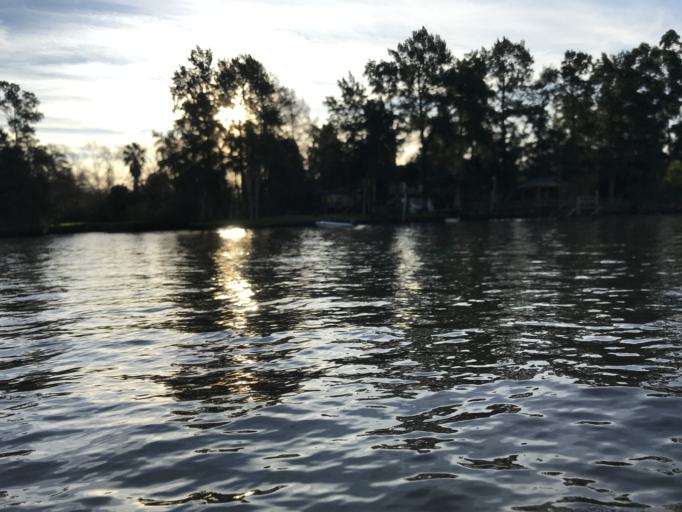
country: AR
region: Buenos Aires
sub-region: Partido de Tigre
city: Tigre
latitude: -34.3819
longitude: -58.5752
